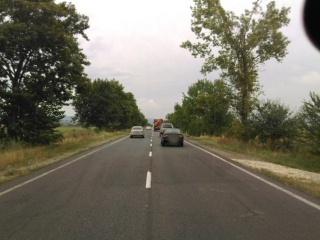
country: BG
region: Plovdiv
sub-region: Obshtina Karlovo
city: Karlovo
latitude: 42.5690
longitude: 24.8275
